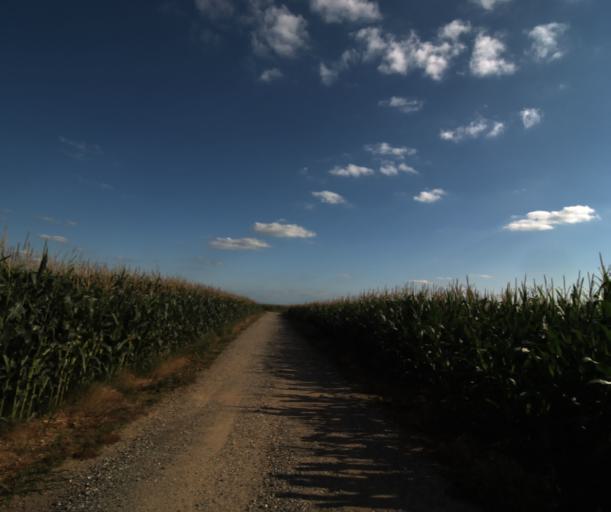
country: FR
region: Midi-Pyrenees
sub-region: Departement de la Haute-Garonne
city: Saint-Lys
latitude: 43.4821
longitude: 1.1962
